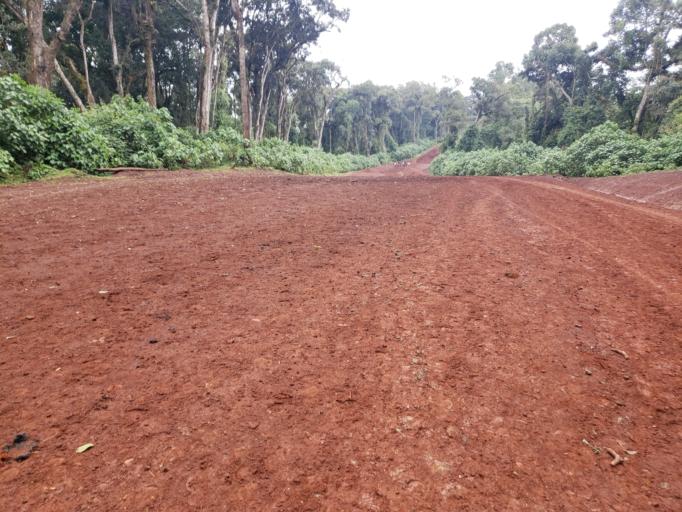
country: ET
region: Oromiya
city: Dodola
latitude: 6.5963
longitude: 39.4124
